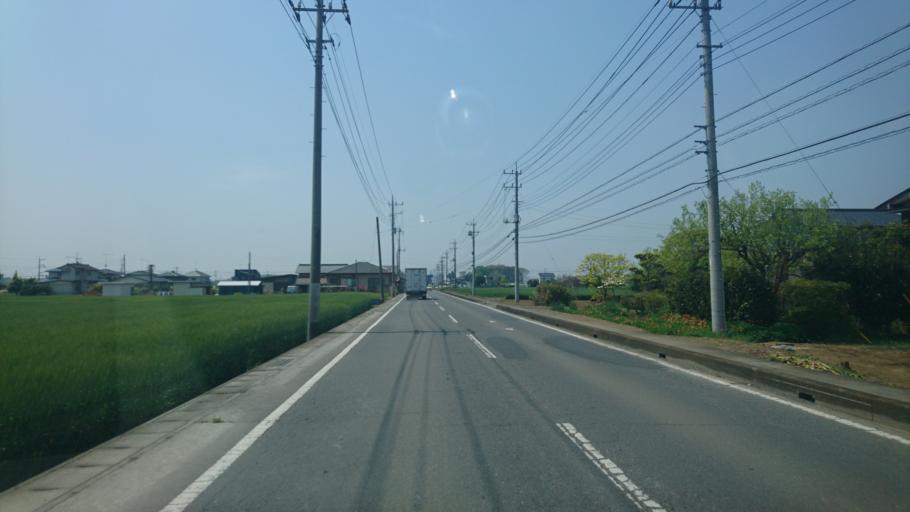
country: JP
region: Ibaraki
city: Shimodate
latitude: 36.2551
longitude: 139.9554
